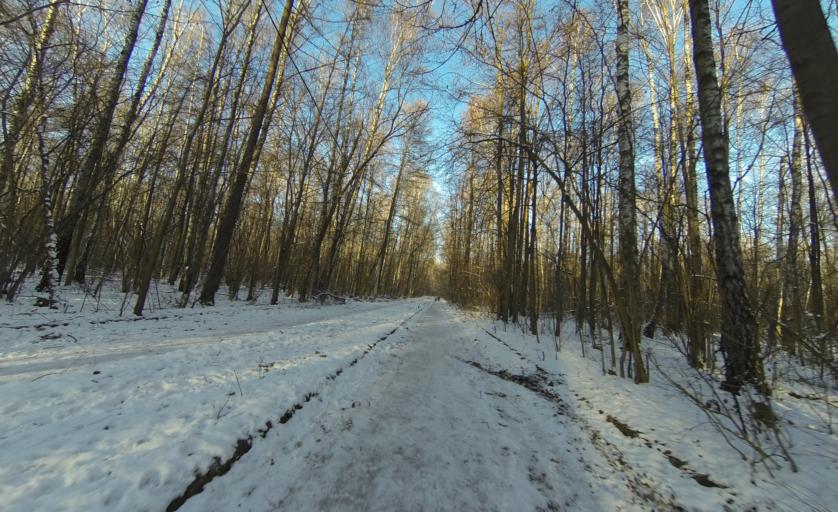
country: RU
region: Moscow
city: Rostokino
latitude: 55.8239
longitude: 37.6846
